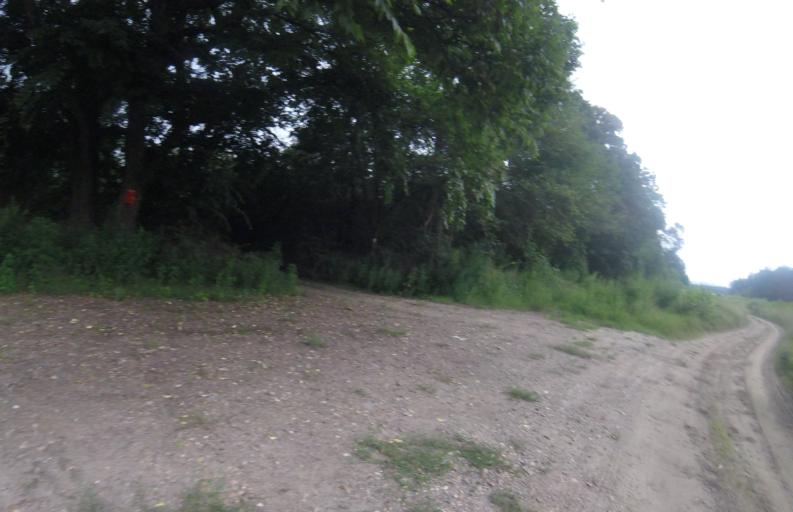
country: HU
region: Pest
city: God
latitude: 47.6716
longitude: 19.1524
